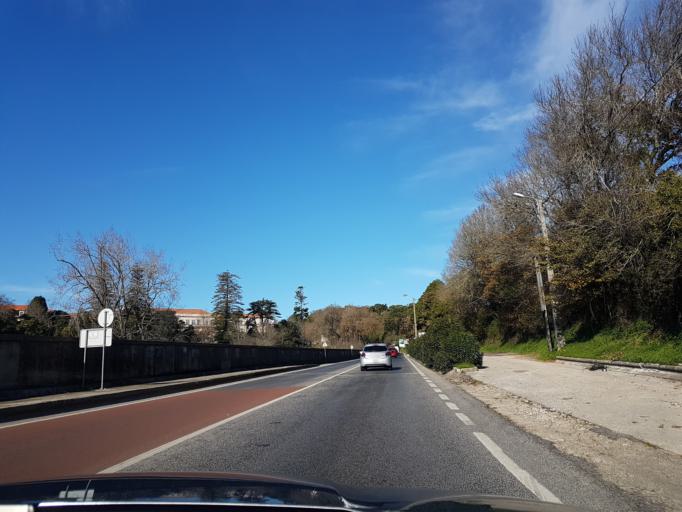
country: PT
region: Lisbon
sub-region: Sintra
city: Sintra
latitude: 38.7841
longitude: -9.3706
